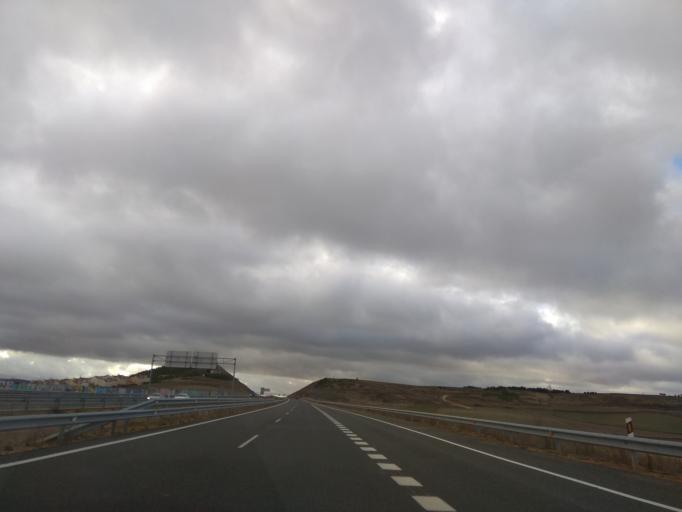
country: ES
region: Castille and Leon
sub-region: Provincia de Burgos
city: Quintanaortuno
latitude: 42.4568
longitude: -3.6893
